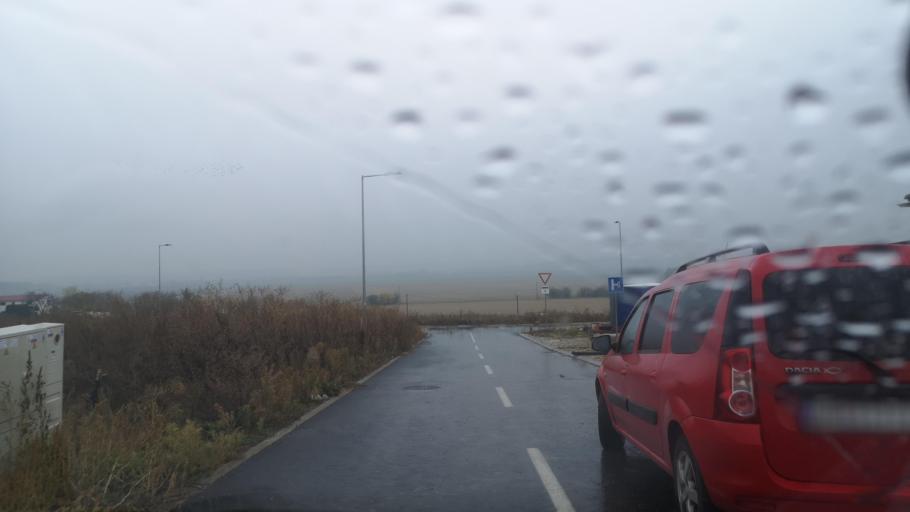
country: SK
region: Nitriansky
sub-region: Okres Nitra
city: Nitra
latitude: 48.2954
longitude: 18.1308
